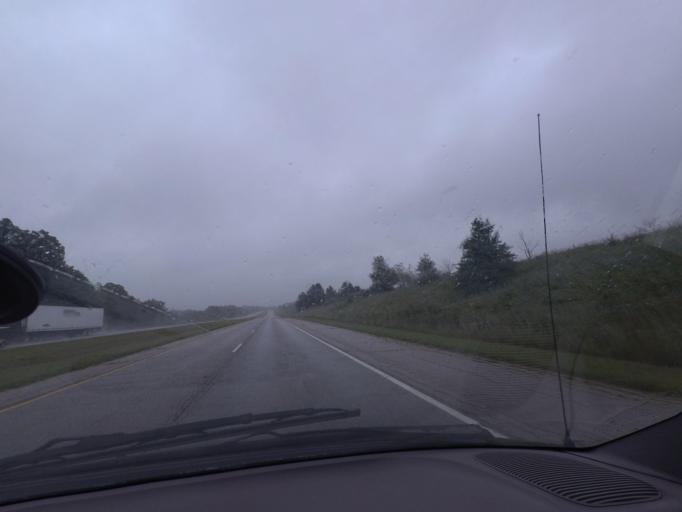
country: US
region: Illinois
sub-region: Pike County
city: Pittsfield
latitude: 39.6876
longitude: -90.8972
